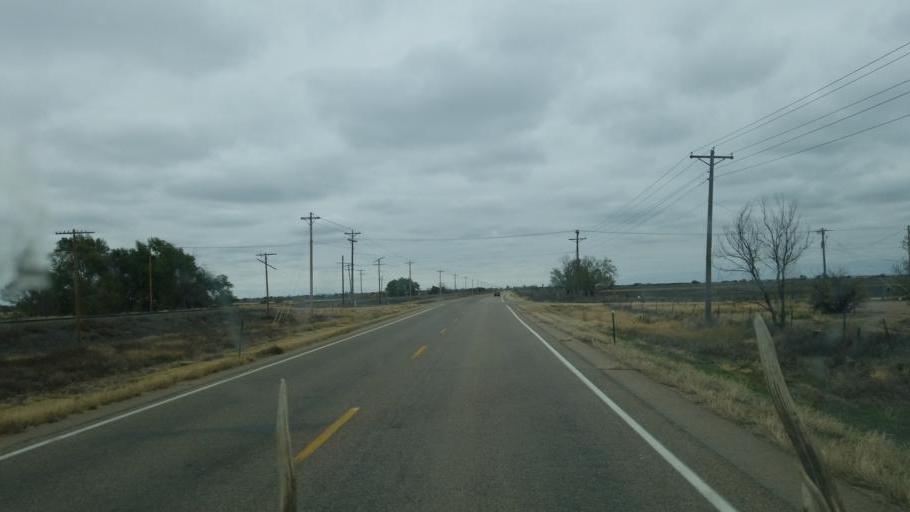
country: US
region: Colorado
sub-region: Crowley County
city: Ordway
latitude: 38.2054
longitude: -103.8046
